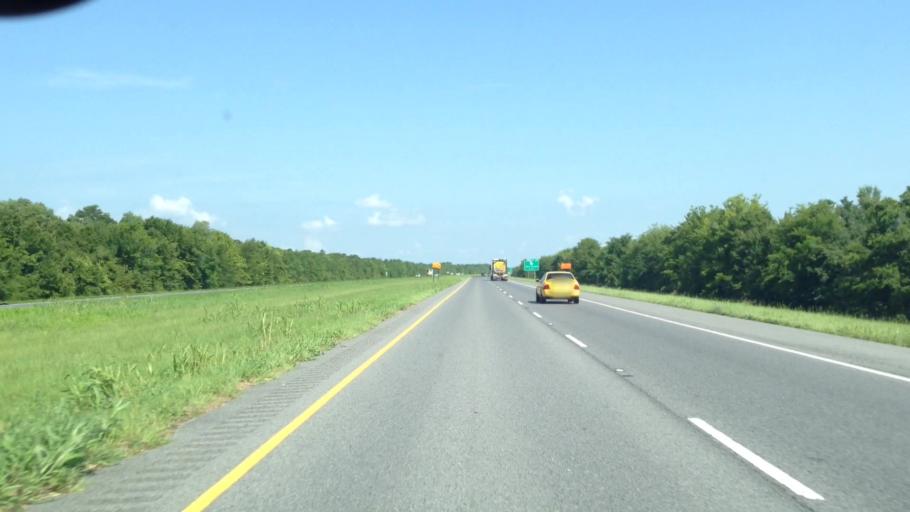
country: US
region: Louisiana
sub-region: Evangeline Parish
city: Ville Platte
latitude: 30.7642
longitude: -92.1718
